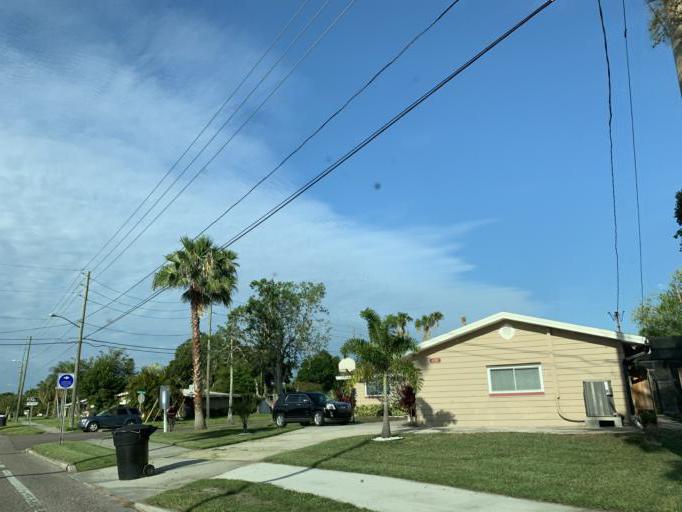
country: US
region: Florida
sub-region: Pinellas County
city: Gandy
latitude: 27.8098
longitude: -82.6017
